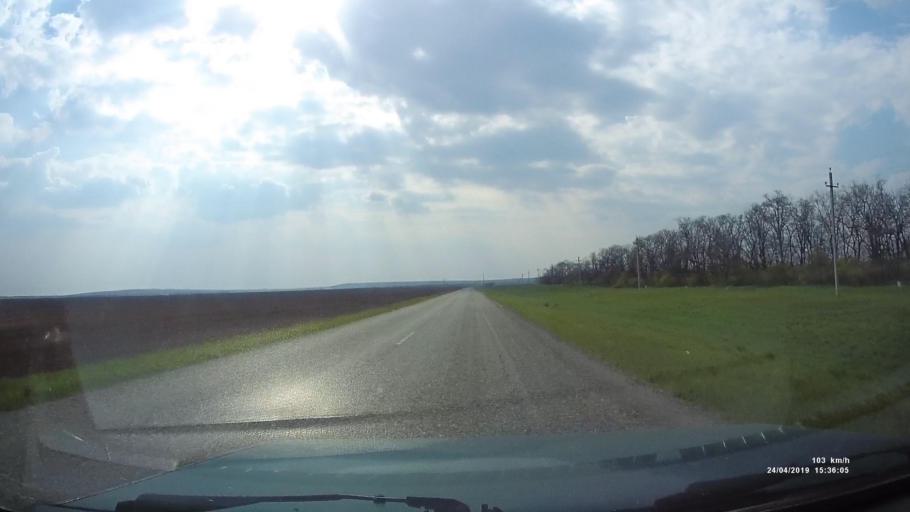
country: RU
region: Kalmykiya
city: Yashalta
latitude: 46.5992
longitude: 42.8793
